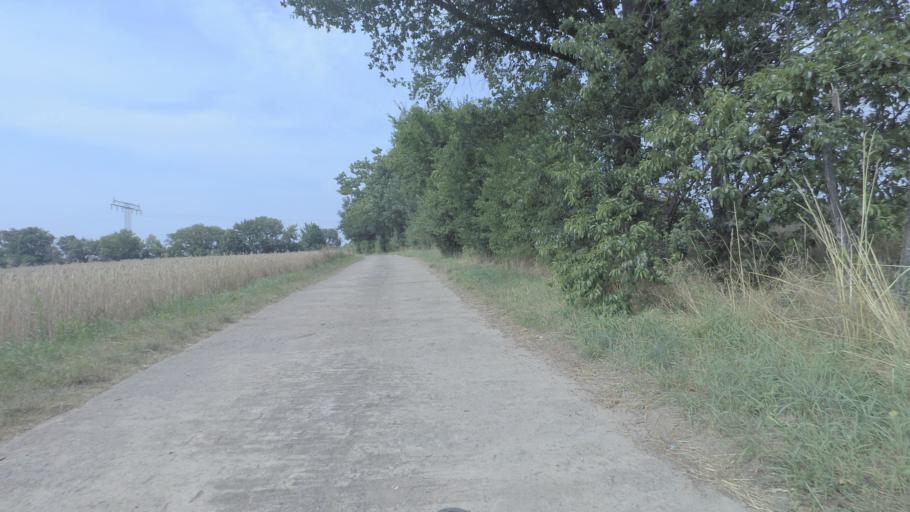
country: DE
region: Brandenburg
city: Rangsdorf
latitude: 52.3354
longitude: 13.4585
